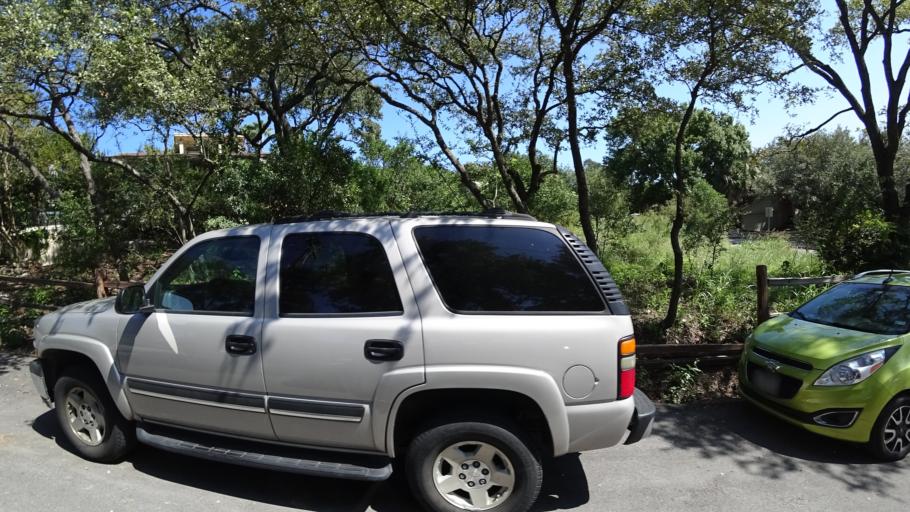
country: US
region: Texas
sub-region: Travis County
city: West Lake Hills
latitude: 30.2986
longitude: -97.7888
